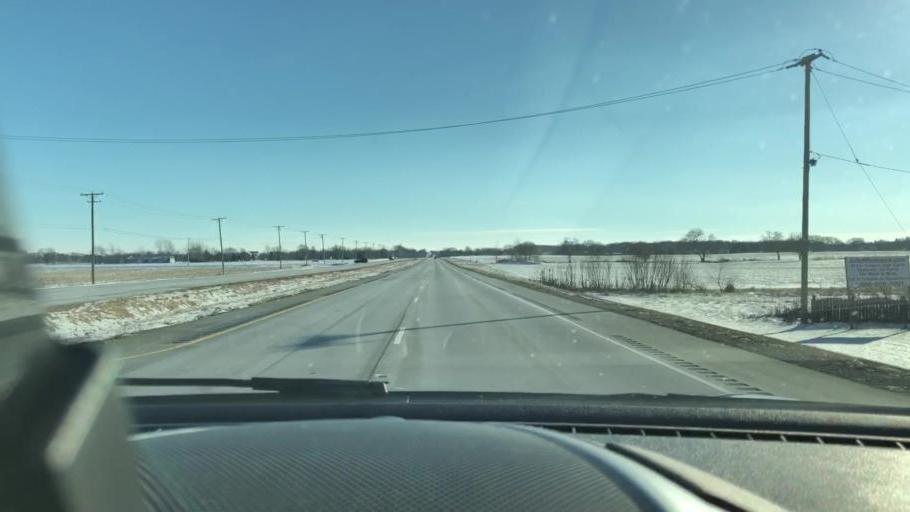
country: US
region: Illinois
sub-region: Will County
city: Preston Heights
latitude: 41.4468
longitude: -88.0792
